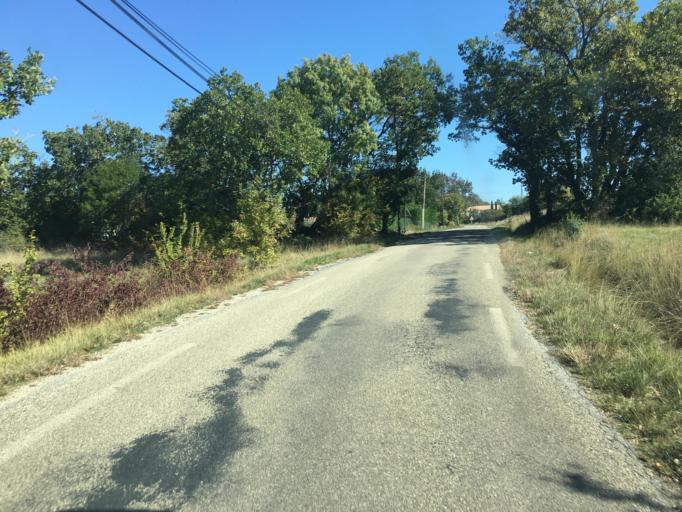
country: FR
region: Languedoc-Roussillon
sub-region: Departement du Gard
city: Barjac
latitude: 44.1640
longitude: 4.3133
